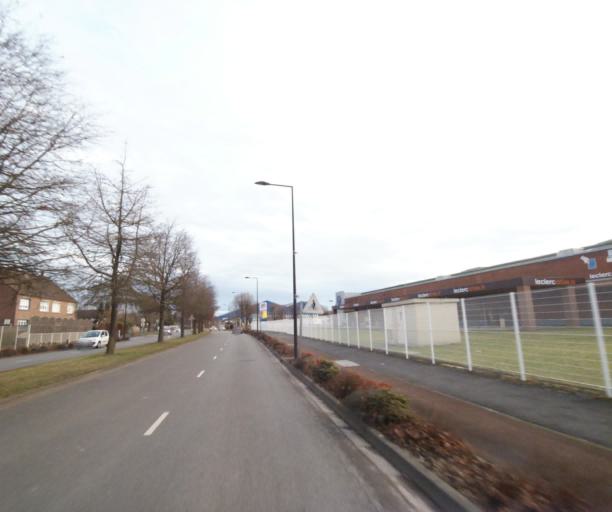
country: FR
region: Nord-Pas-de-Calais
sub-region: Departement du Nord
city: Saint-Saulve
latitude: 50.3737
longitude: 3.5382
